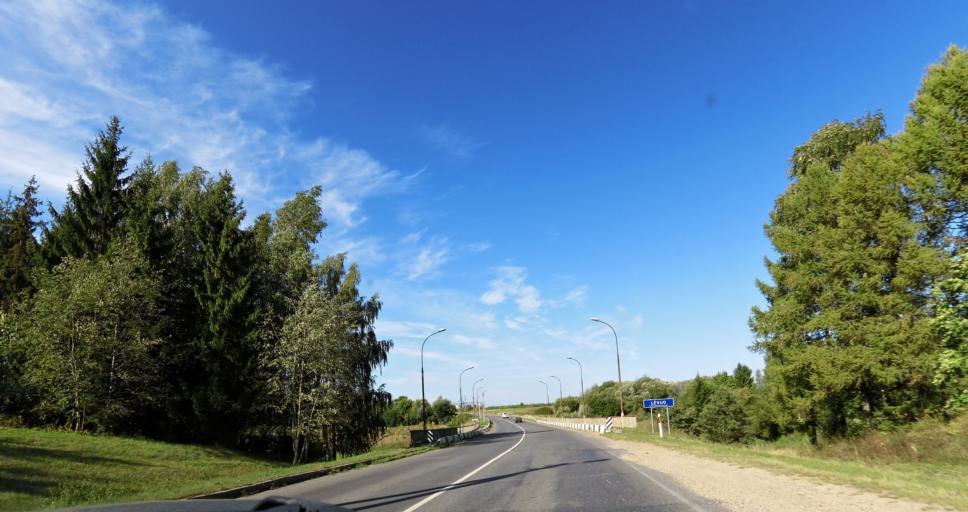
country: LT
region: Panevezys
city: Pasvalys
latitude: 56.0700
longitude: 24.4266
